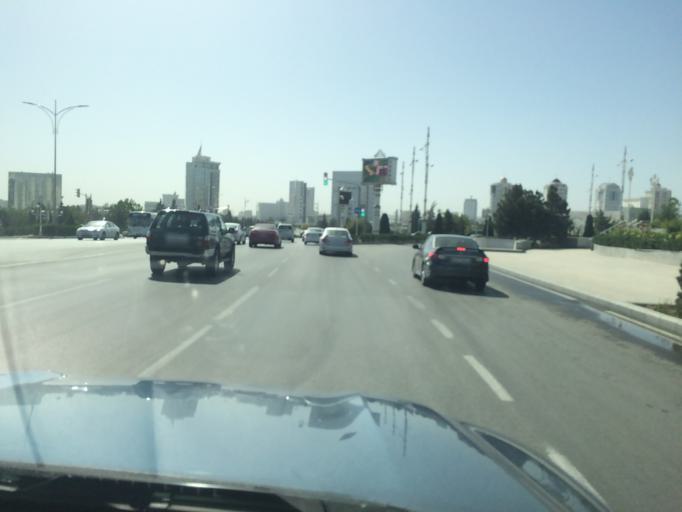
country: TM
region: Ahal
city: Ashgabat
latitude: 37.9276
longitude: 58.3711
